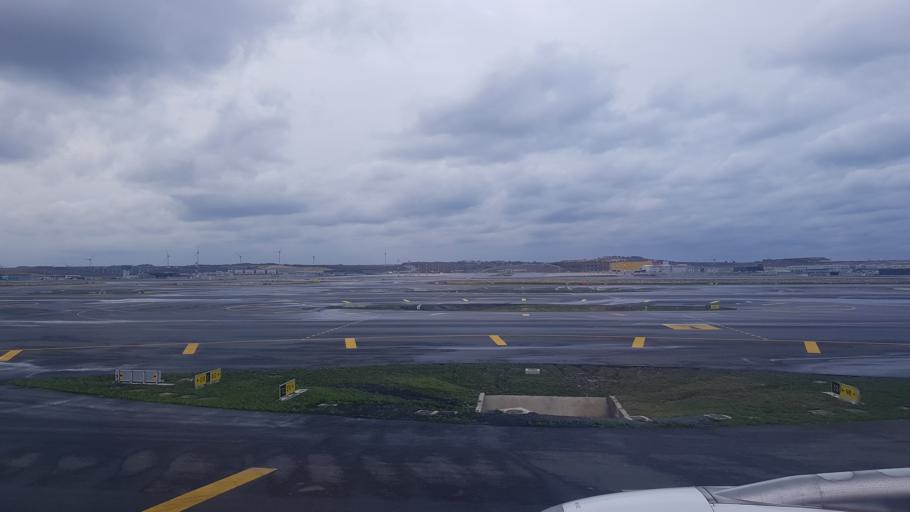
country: TR
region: Istanbul
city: Durusu
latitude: 41.2680
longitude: 28.7334
